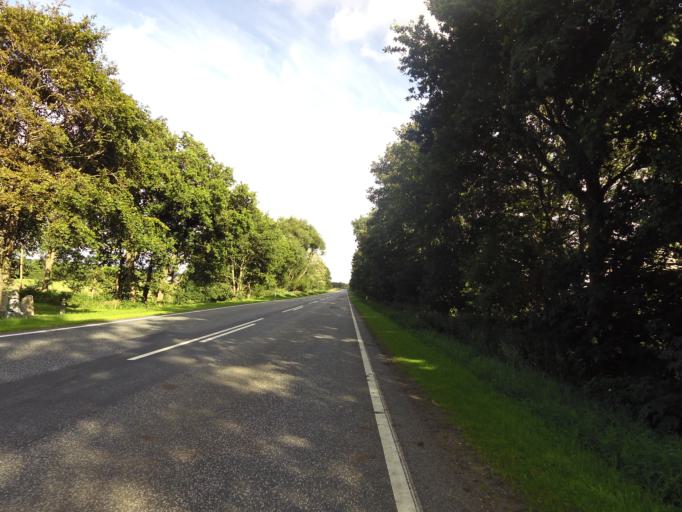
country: DK
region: South Denmark
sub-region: Tonder Kommune
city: Toftlund
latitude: 55.2185
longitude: 9.0207
